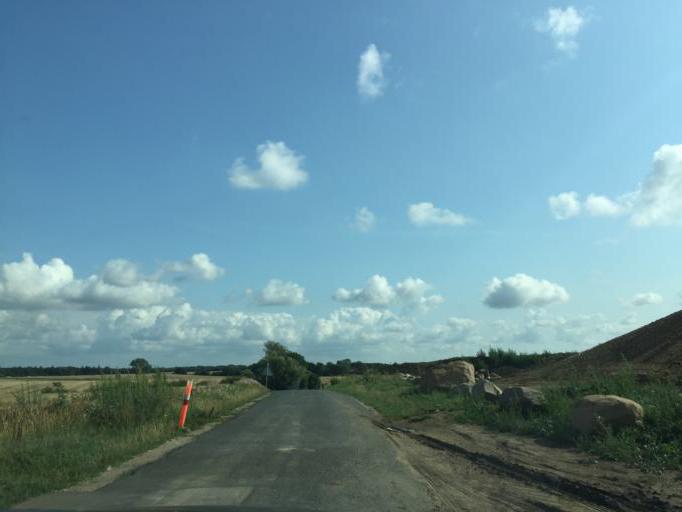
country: DK
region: South Denmark
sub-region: Odense Kommune
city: Bellinge
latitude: 55.3258
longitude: 10.3710
